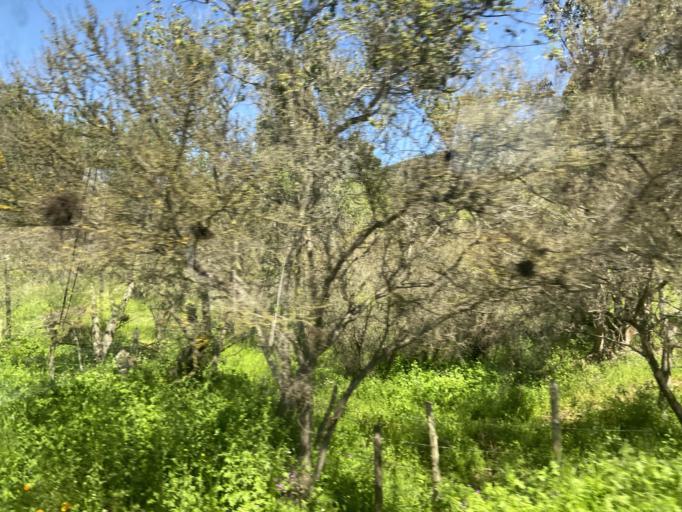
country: CL
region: Valparaiso
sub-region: Provincia de Marga Marga
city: Villa Alemana
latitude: -33.1809
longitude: -71.3059
